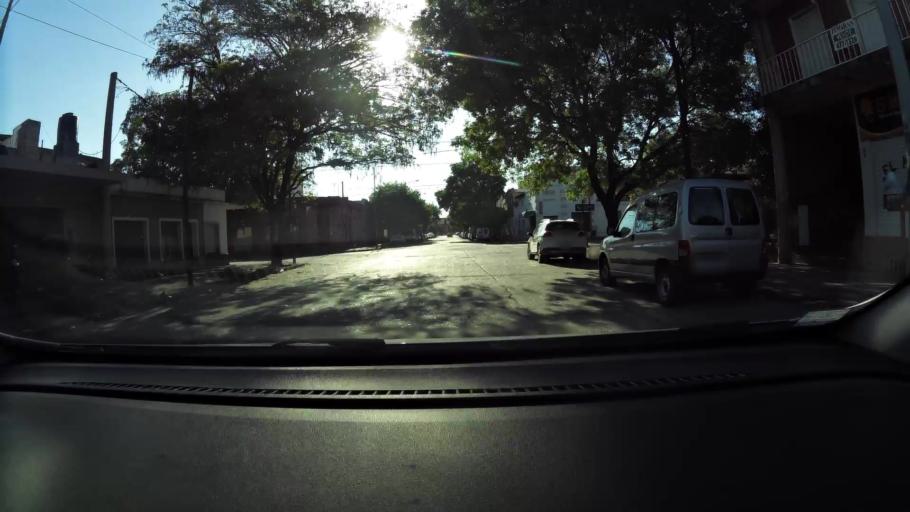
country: AR
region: Cordoba
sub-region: Departamento de Capital
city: Cordoba
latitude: -31.3876
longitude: -64.1876
